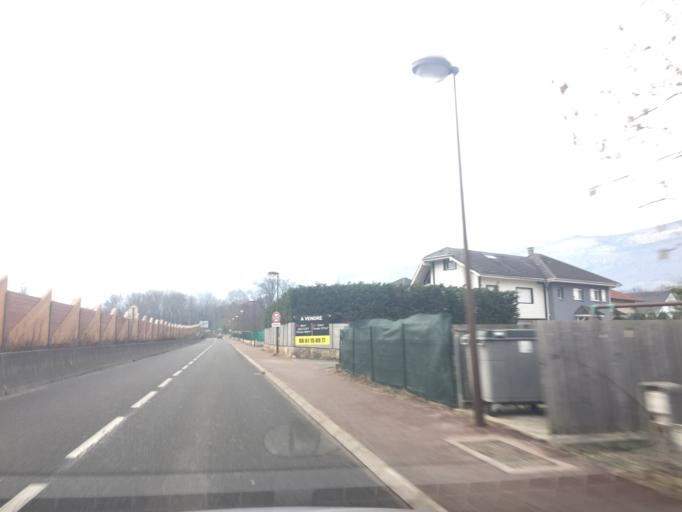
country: FR
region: Rhone-Alpes
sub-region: Departement de la Savoie
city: Voglans
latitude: 45.6192
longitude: 5.8855
